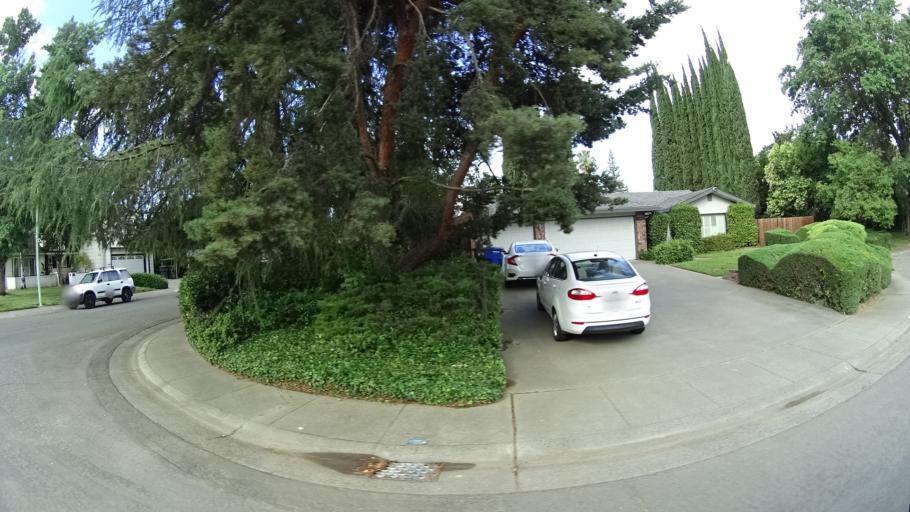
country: US
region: California
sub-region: Sacramento County
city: Rosemont
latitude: 38.5570
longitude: -121.3992
